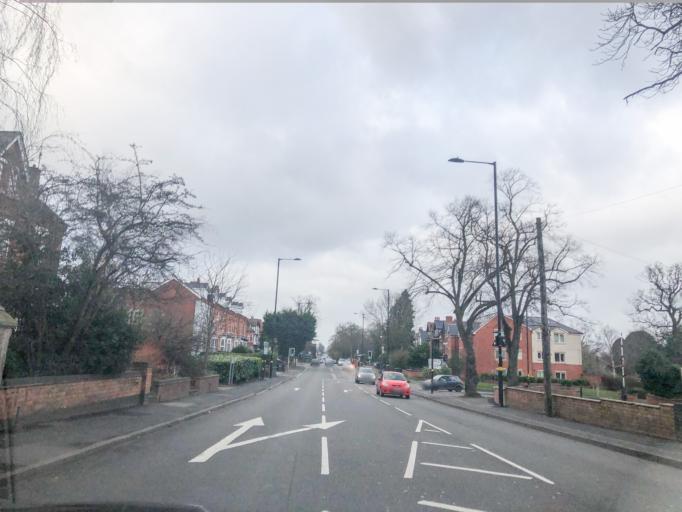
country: GB
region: England
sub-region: Solihull
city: Tidbury Green
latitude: 52.4246
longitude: -1.8924
